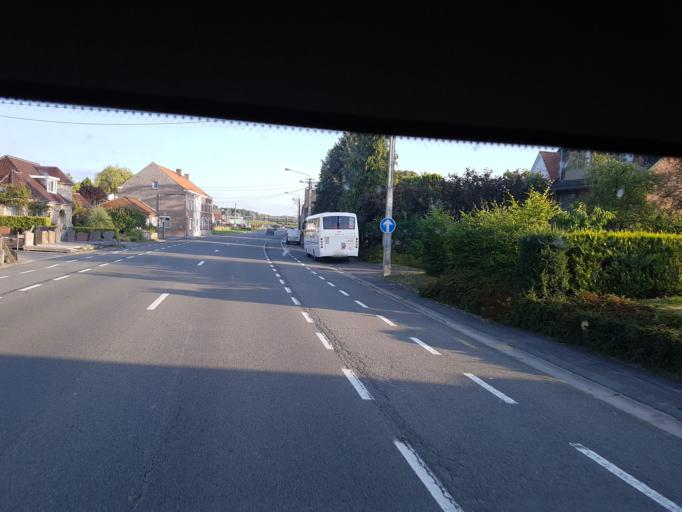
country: BE
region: Wallonia
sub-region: Province du Hainaut
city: Antoing
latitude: 50.5524
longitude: 3.4303
